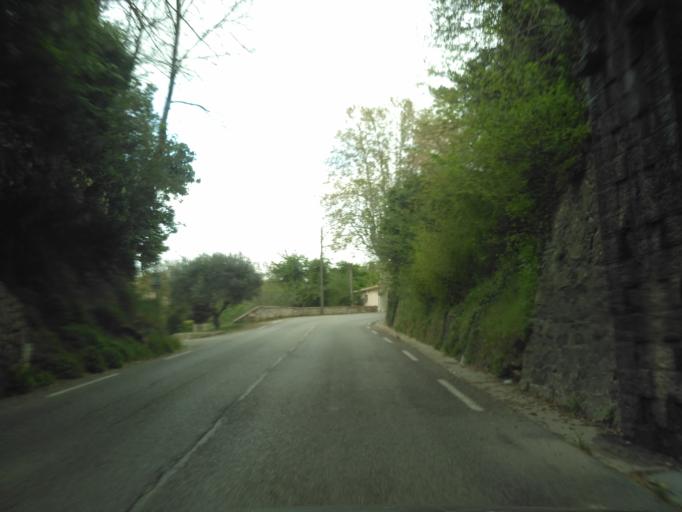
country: FR
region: Provence-Alpes-Cote d'Azur
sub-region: Departement du Var
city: Barjols
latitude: 43.5596
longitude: 6.0070
